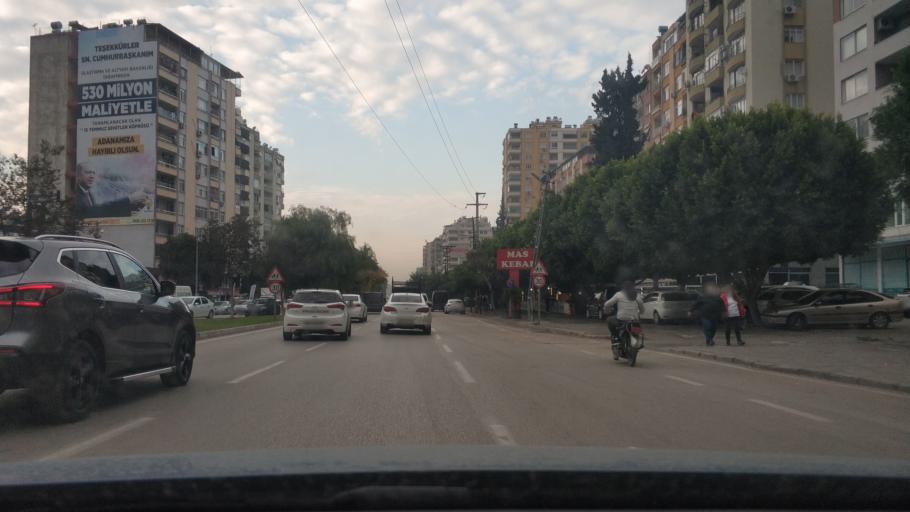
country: TR
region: Adana
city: Adana
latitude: 36.9979
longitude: 35.3181
